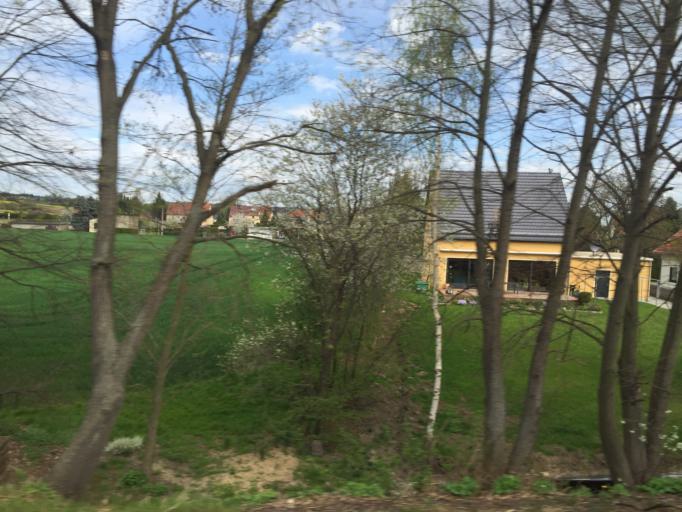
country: DE
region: Saxony
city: Bautzen
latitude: 51.1773
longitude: 14.3919
